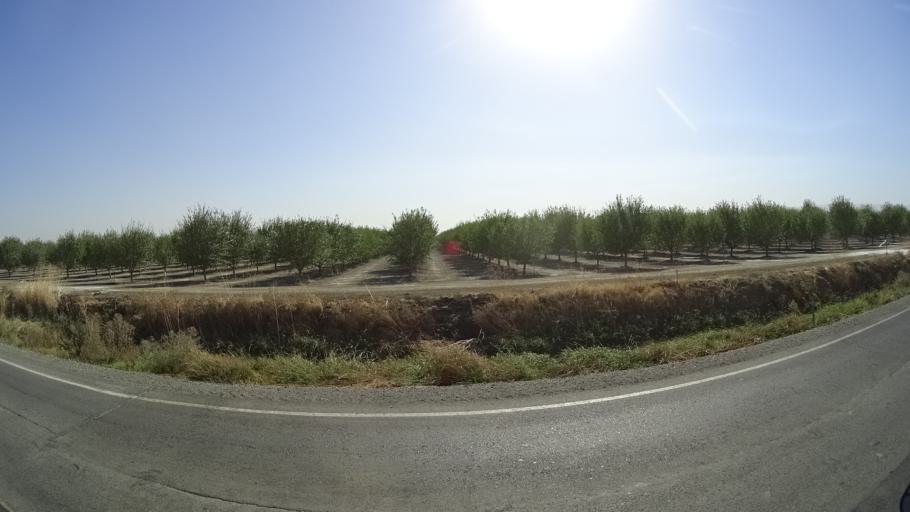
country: US
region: California
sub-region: Yolo County
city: Esparto
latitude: 38.7307
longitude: -121.9881
